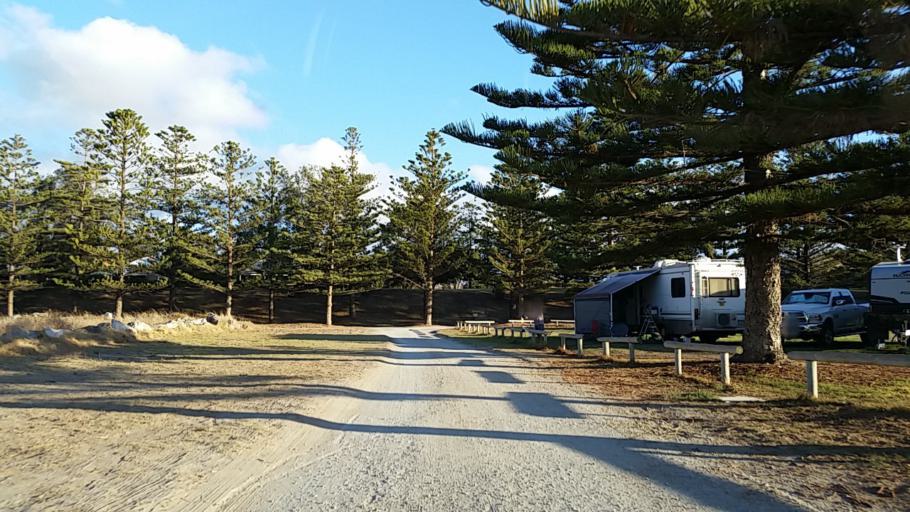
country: AU
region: South Australia
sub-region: Yankalilla
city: Normanville
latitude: -35.5245
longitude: 138.1927
